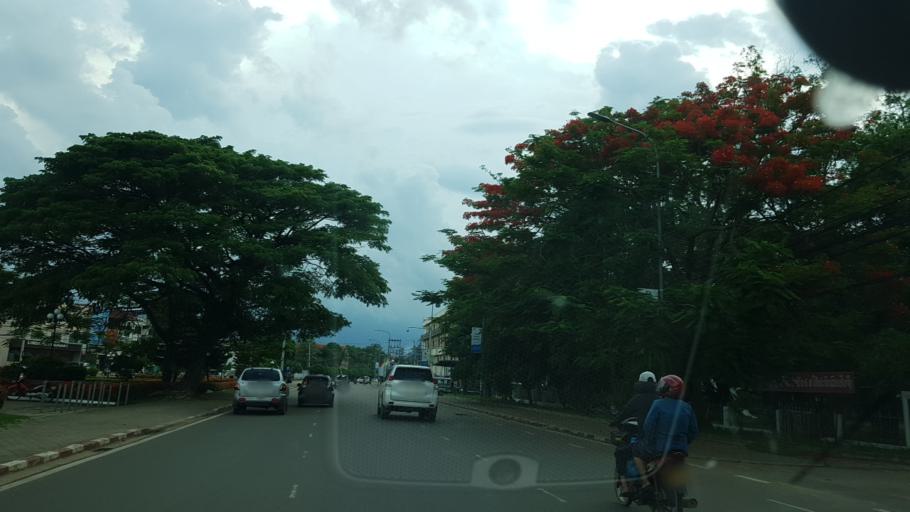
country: LA
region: Vientiane
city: Vientiane
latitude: 17.9688
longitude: 102.5957
